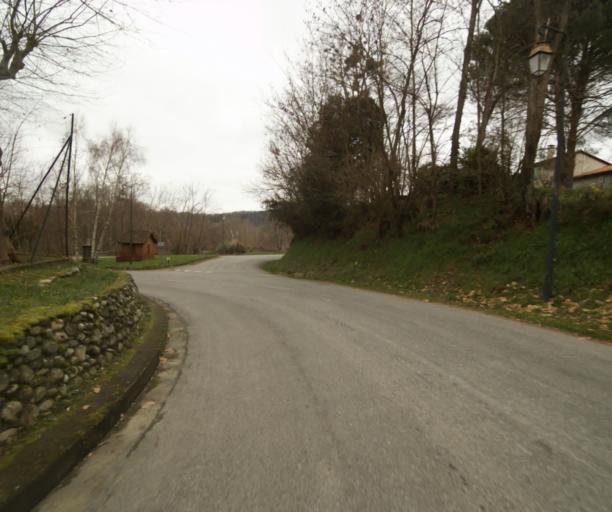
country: FR
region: Midi-Pyrenees
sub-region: Departement de l'Ariege
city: Pamiers
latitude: 43.1653
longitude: 1.5982
